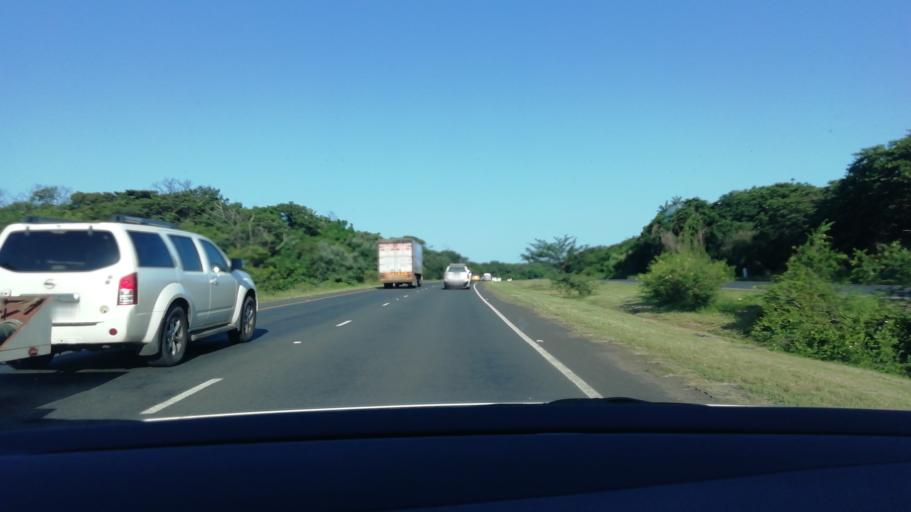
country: ZA
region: KwaZulu-Natal
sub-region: uThungulu District Municipality
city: Richards Bay
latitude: -28.7678
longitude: 32.0512
